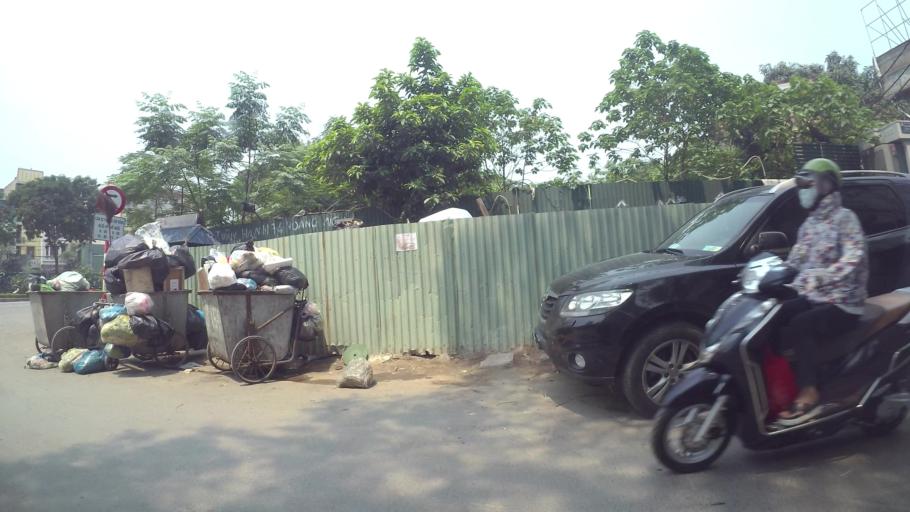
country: VN
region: Ha Noi
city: Thanh Xuan
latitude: 21.0078
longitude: 105.8090
